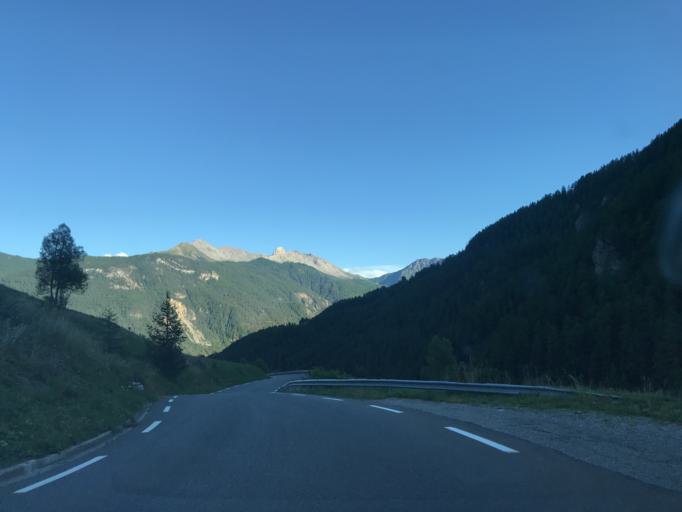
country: FR
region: Provence-Alpes-Cote d'Azur
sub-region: Departement des Hautes-Alpes
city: Guillestre
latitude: 44.7596
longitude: 6.7462
